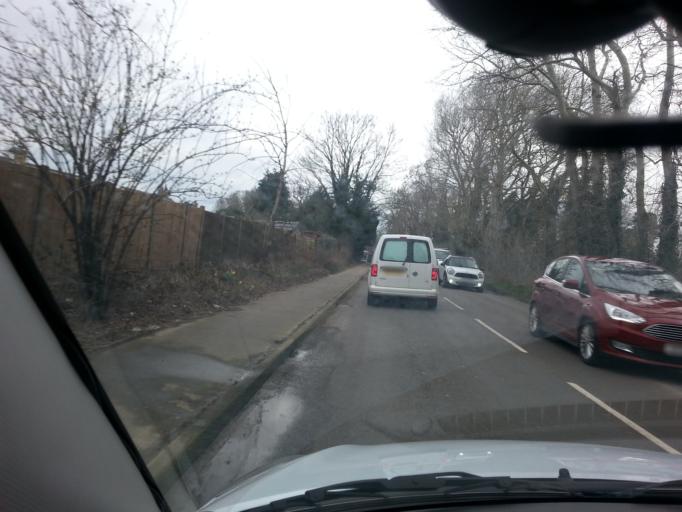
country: GB
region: England
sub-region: Norfolk
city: Weeting
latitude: 52.4634
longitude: 0.6198
